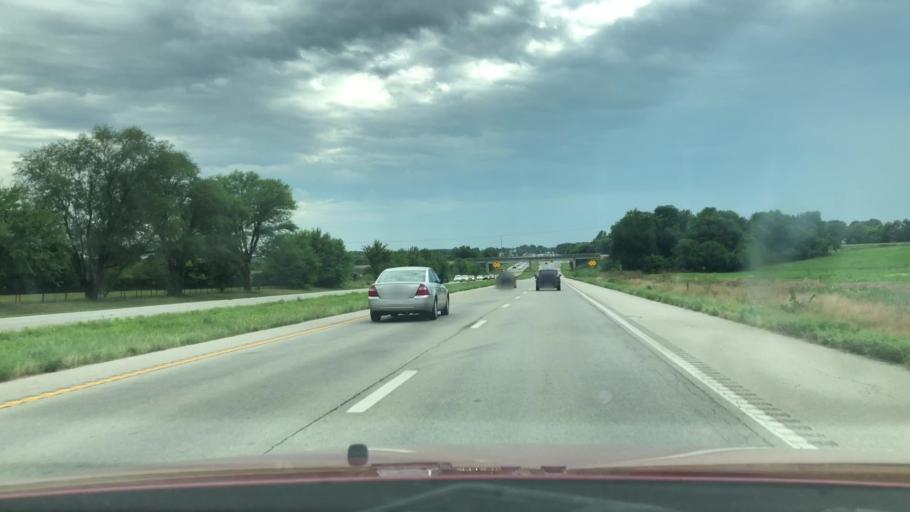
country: US
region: Missouri
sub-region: Greene County
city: Battlefield
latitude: 37.1516
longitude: -93.4181
